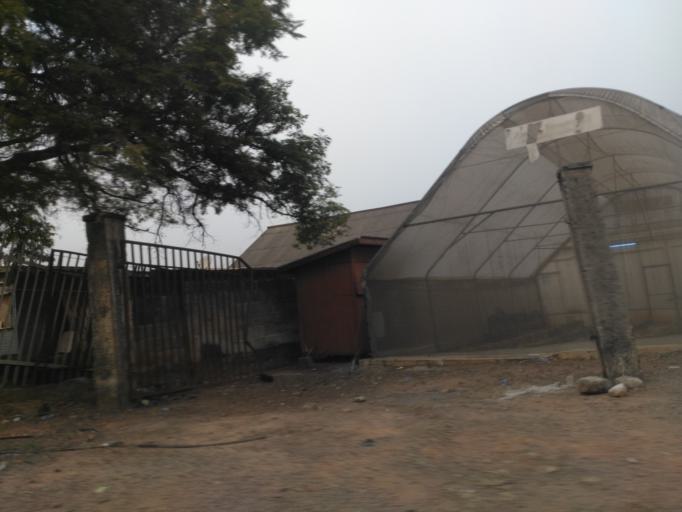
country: GH
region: Ashanti
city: Kumasi
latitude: 6.6799
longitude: -1.6122
